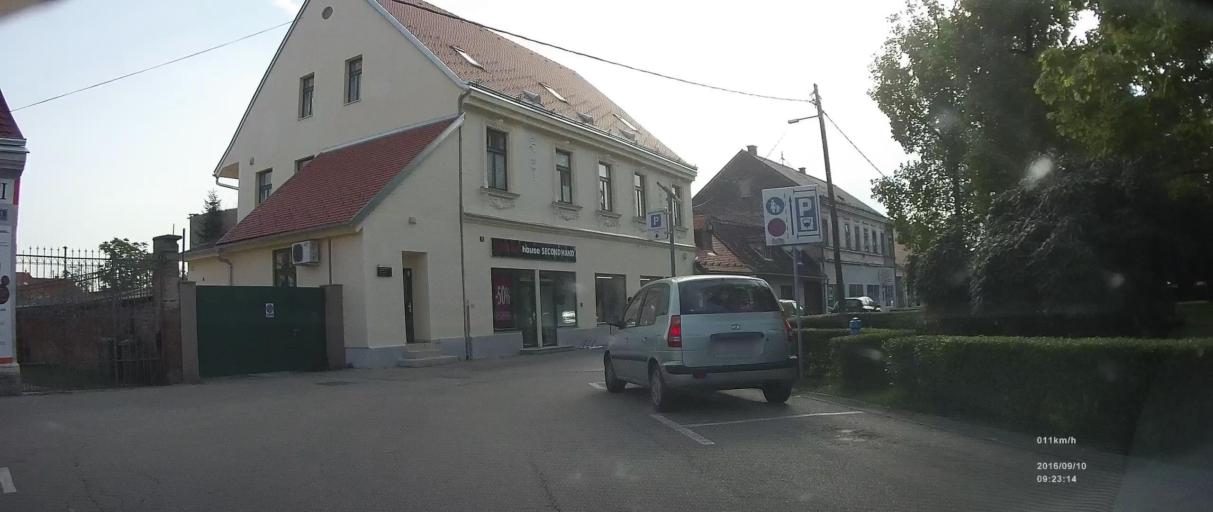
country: HR
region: Zagrebacka
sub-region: Grad Velika Gorica
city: Velika Gorica
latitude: 45.7136
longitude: 16.0766
